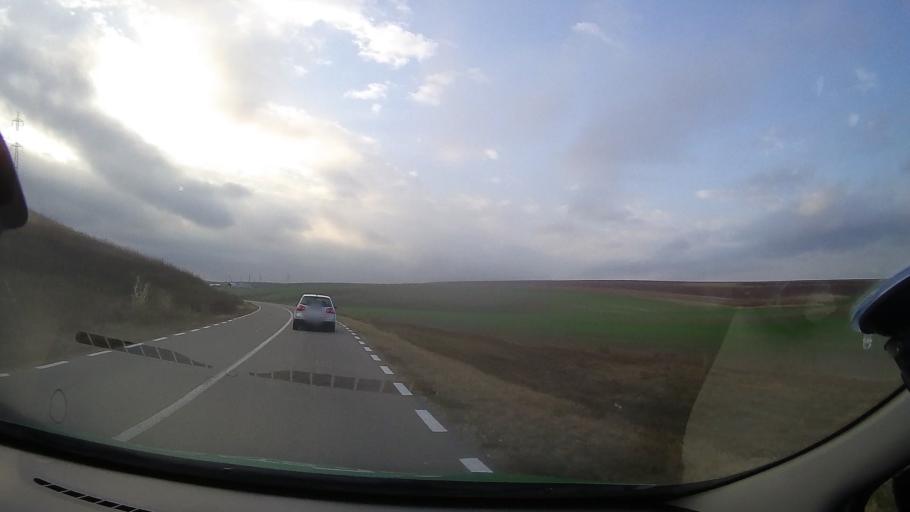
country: RO
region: Constanta
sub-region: Comuna Pestera
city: Pestera
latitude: 44.2032
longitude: 28.1476
